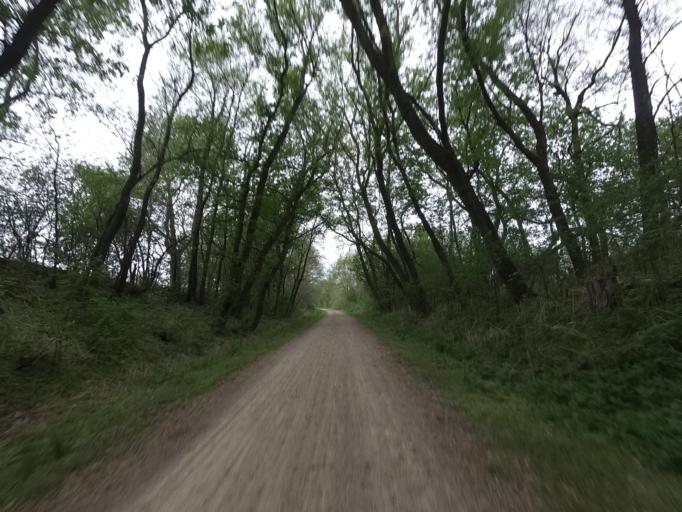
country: US
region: Wisconsin
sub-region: Jefferson County
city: Lake Mills
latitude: 43.0603
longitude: -88.8792
